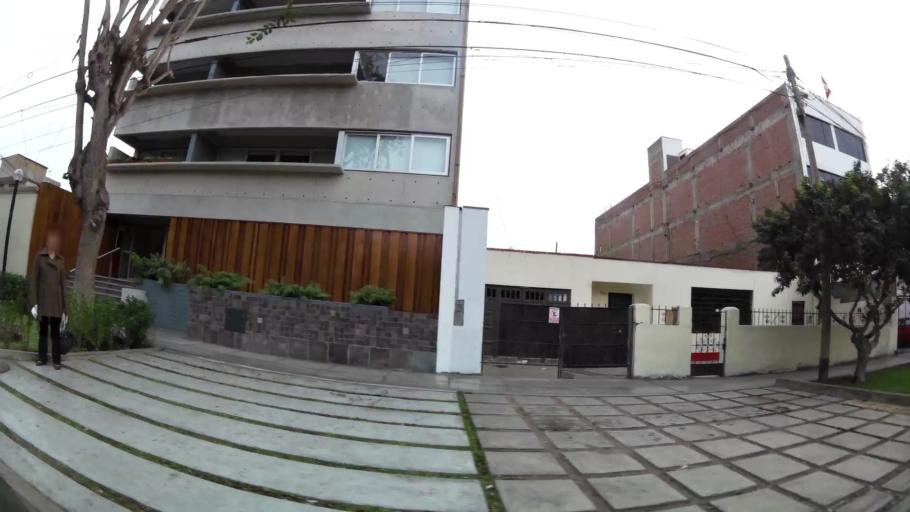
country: PE
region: Lima
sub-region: Lima
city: San Isidro
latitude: -12.1103
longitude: -77.0474
